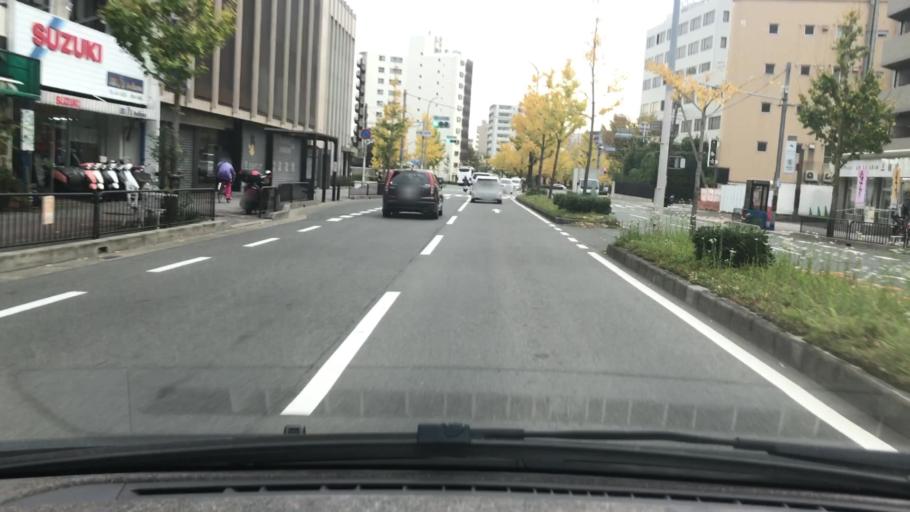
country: JP
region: Kyoto
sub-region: Kyoto-shi
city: Kamigyo-ku
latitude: 35.0388
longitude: 135.7518
